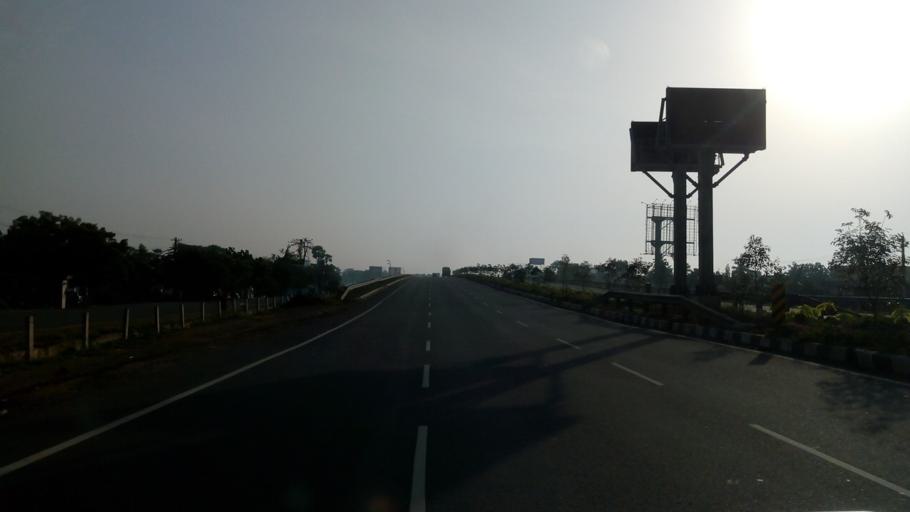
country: IN
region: Andhra Pradesh
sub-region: Guntur
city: Mangalagiri
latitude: 16.3932
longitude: 80.5425
